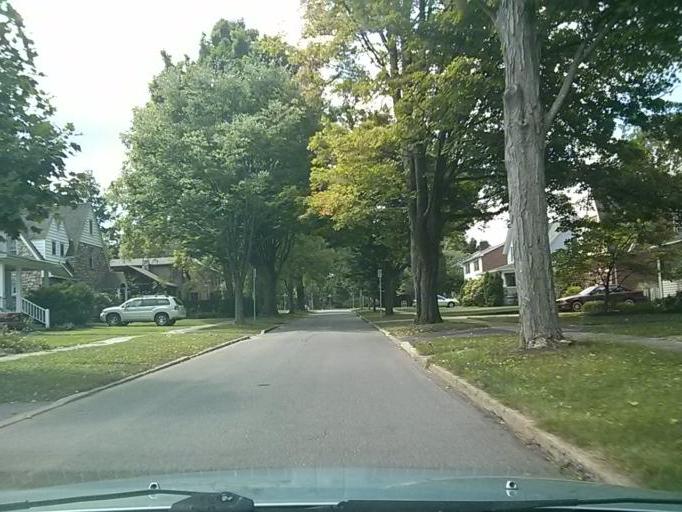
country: US
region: Pennsylvania
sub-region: Centre County
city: State College
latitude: 40.8015
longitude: -77.8703
